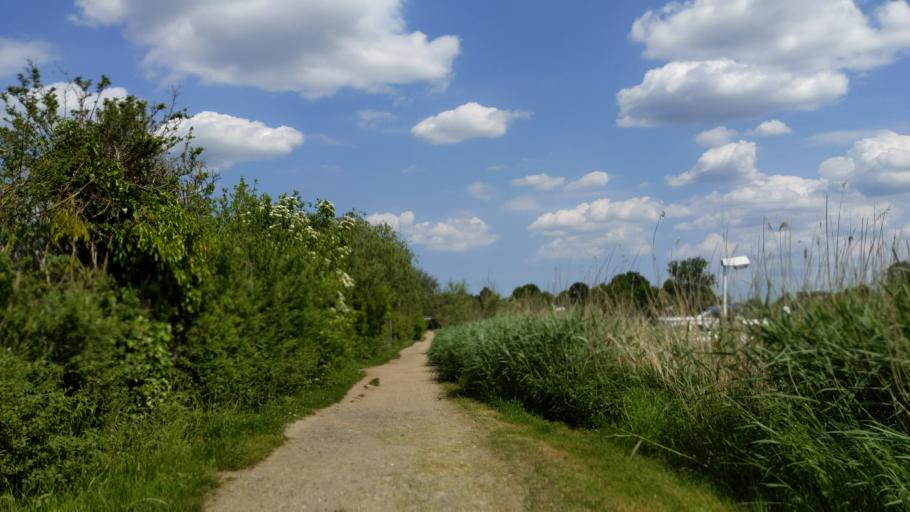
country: DE
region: Schleswig-Holstein
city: Luebeck
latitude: 53.8545
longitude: 10.6753
